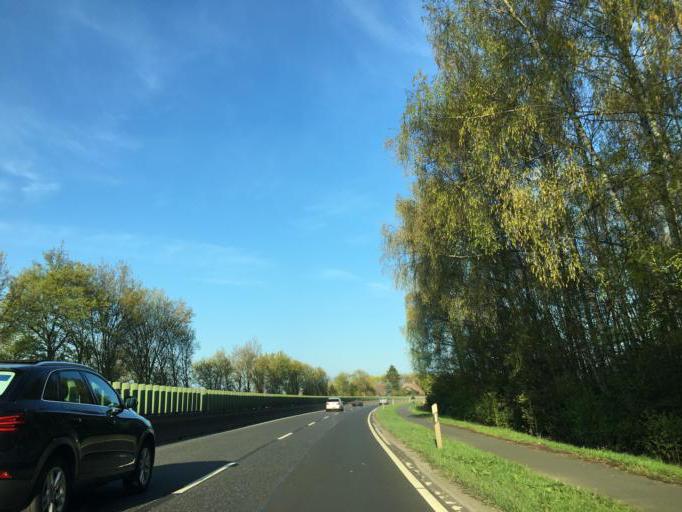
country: DE
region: Hesse
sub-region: Regierungsbezirk Darmstadt
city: Offenbach
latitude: 50.1391
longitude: 8.7843
